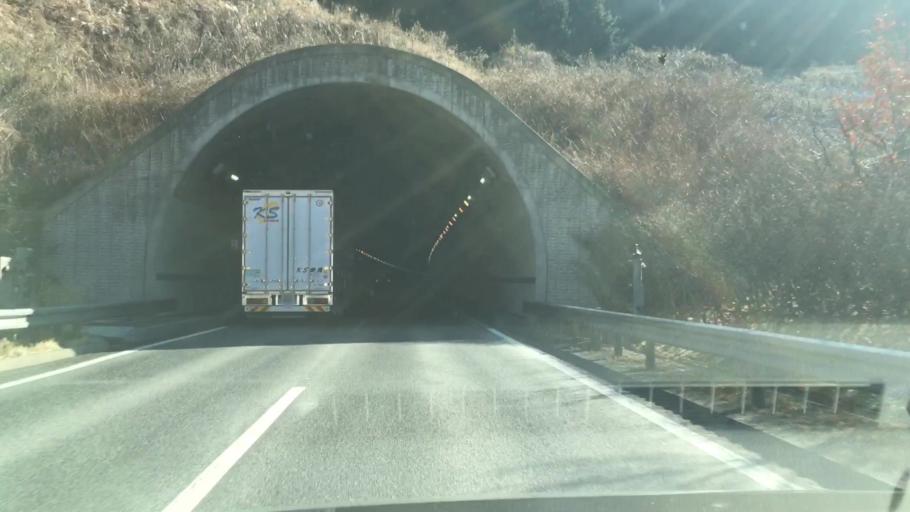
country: JP
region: Nagano
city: Nagano-shi
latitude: 36.5093
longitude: 138.1587
